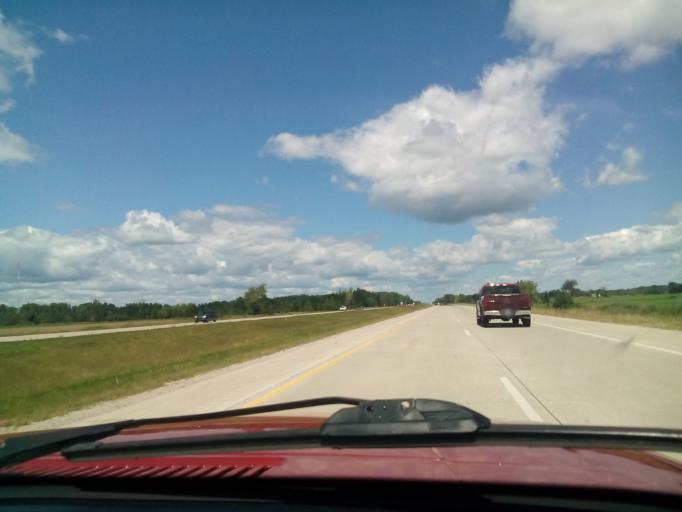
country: US
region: Michigan
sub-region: Bay County
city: Pinconning
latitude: 43.8139
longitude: -84.0204
